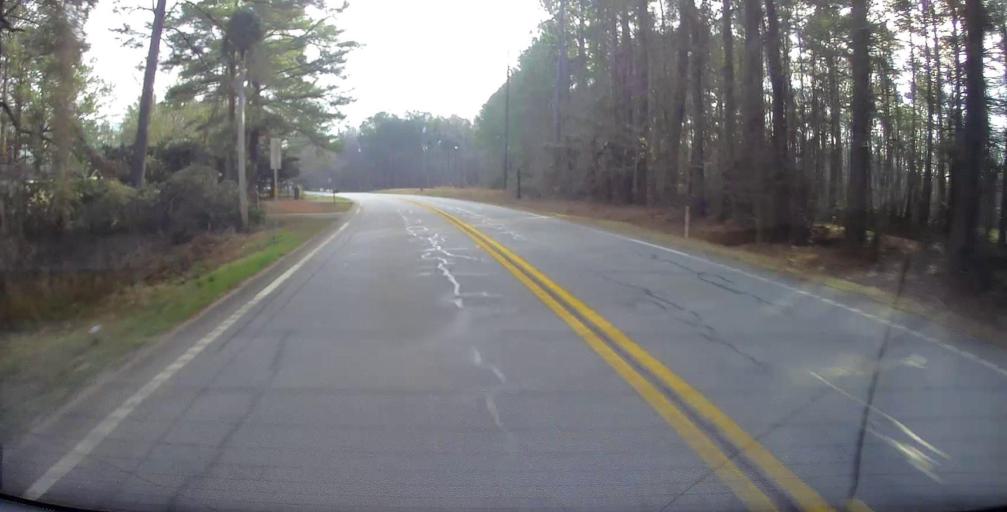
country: US
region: Georgia
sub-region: Harris County
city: Hamilton
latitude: 32.7315
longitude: -84.8744
